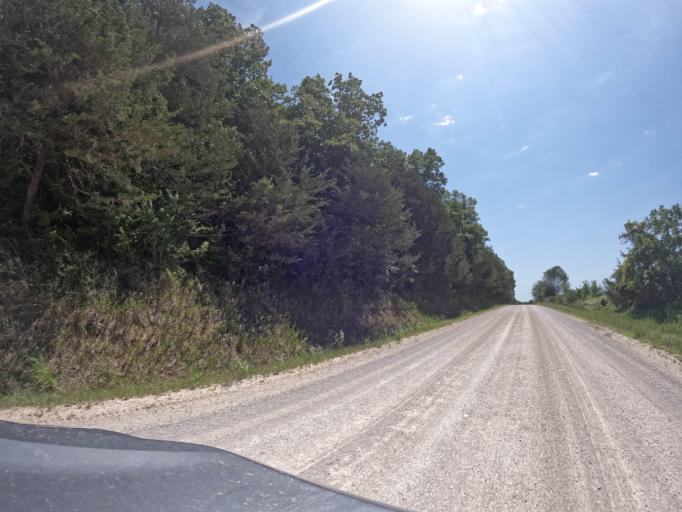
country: US
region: Iowa
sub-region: Henry County
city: Mount Pleasant
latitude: 40.8852
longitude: -91.5353
